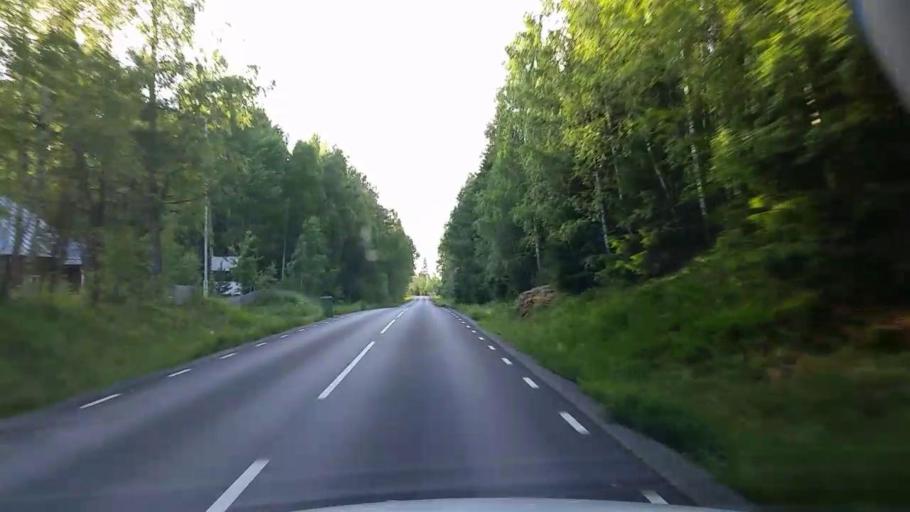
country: SE
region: Vaestmanland
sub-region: Kopings Kommun
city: Kolsva
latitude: 59.6600
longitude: 15.8368
